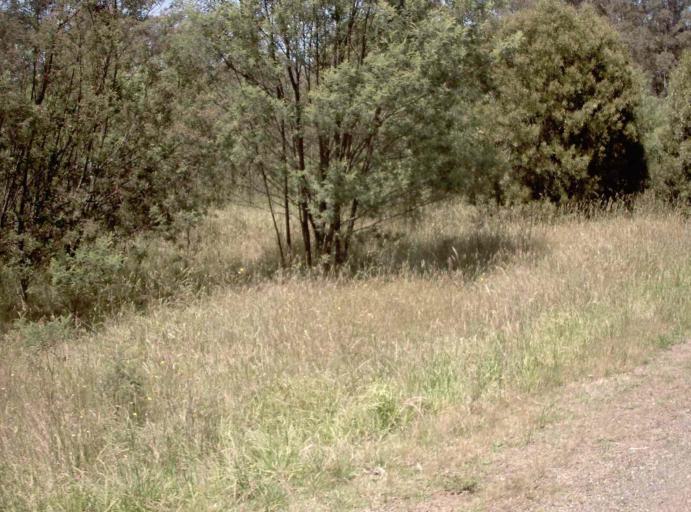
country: AU
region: Victoria
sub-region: East Gippsland
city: Bairnsdale
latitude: -37.4032
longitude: 147.8349
